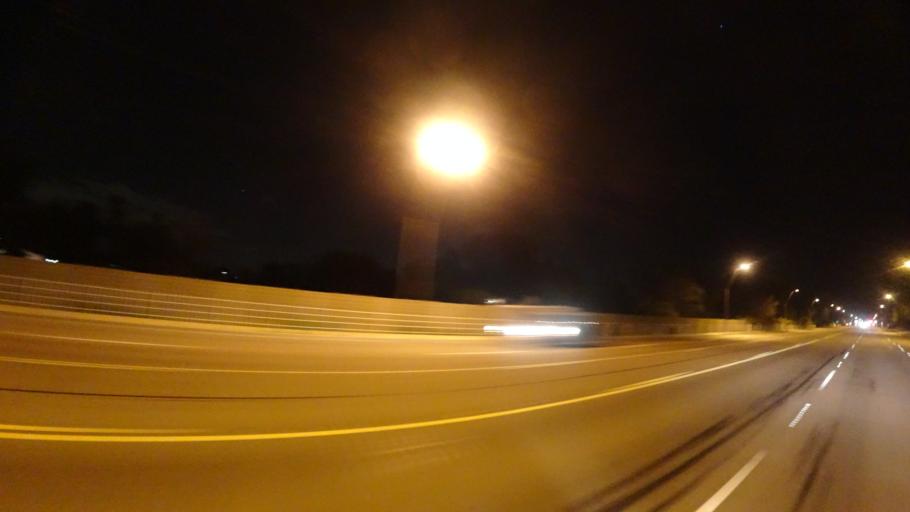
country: US
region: Arizona
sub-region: Maricopa County
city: Guadalupe
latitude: 33.3336
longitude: -111.9285
